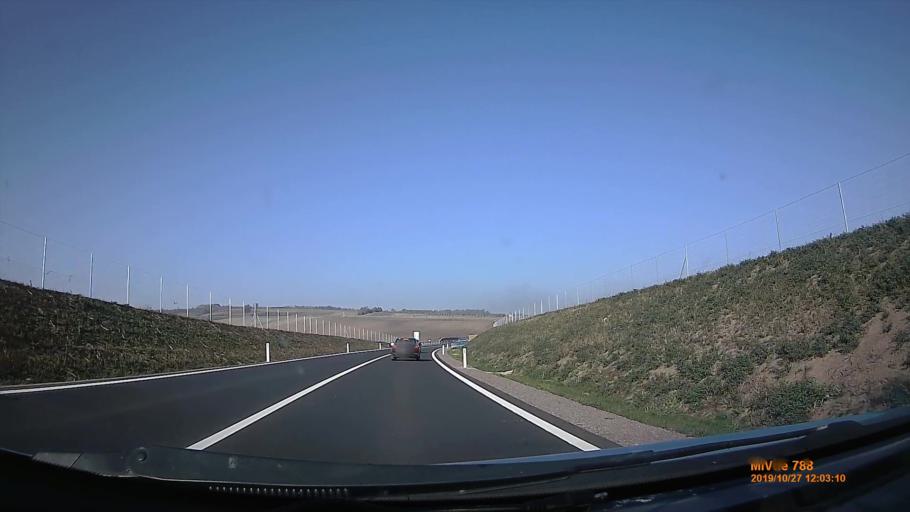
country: AT
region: Lower Austria
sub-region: Politischer Bezirk Mistelbach
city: Drasenhofen
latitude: 48.7400
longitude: 16.6395
